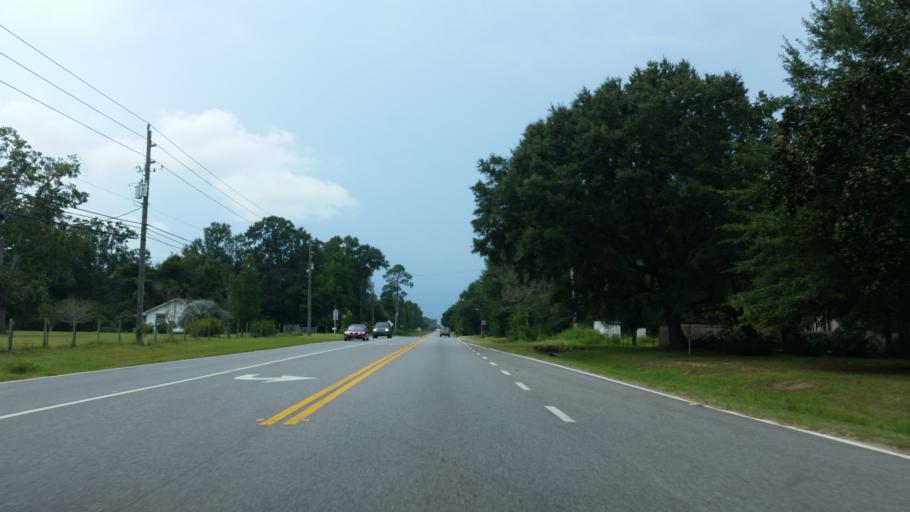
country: US
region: Florida
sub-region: Santa Rosa County
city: Pace
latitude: 30.6337
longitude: -87.1719
